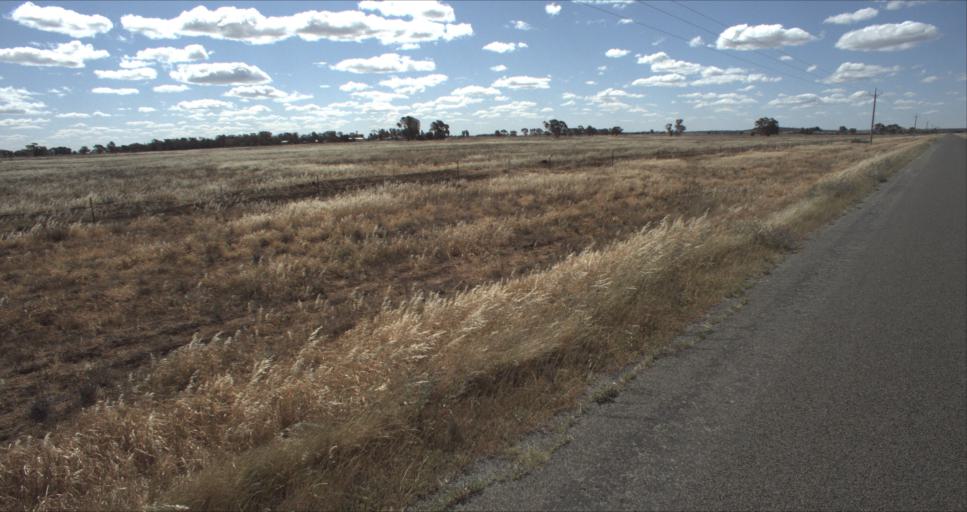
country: AU
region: New South Wales
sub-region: Leeton
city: Leeton
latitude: -34.4694
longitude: 146.2512
